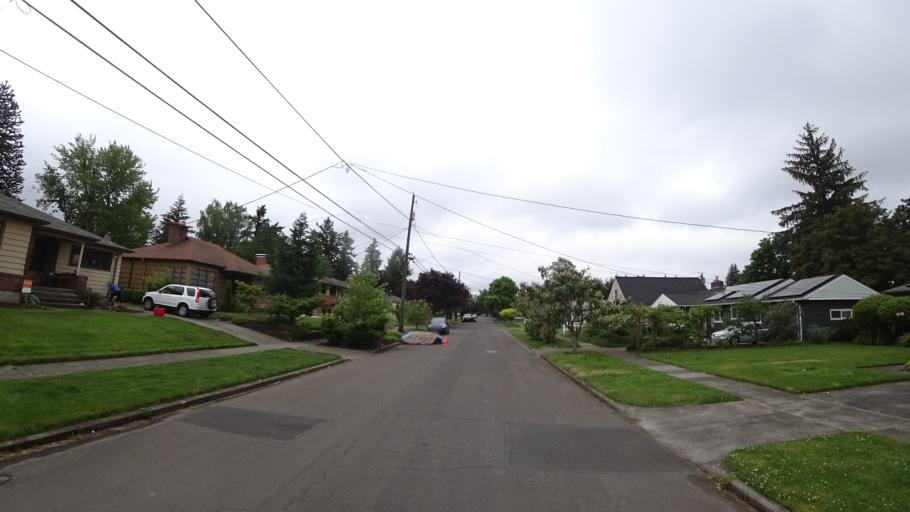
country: US
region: Oregon
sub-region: Multnomah County
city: Portland
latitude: 45.5519
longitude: -122.6169
